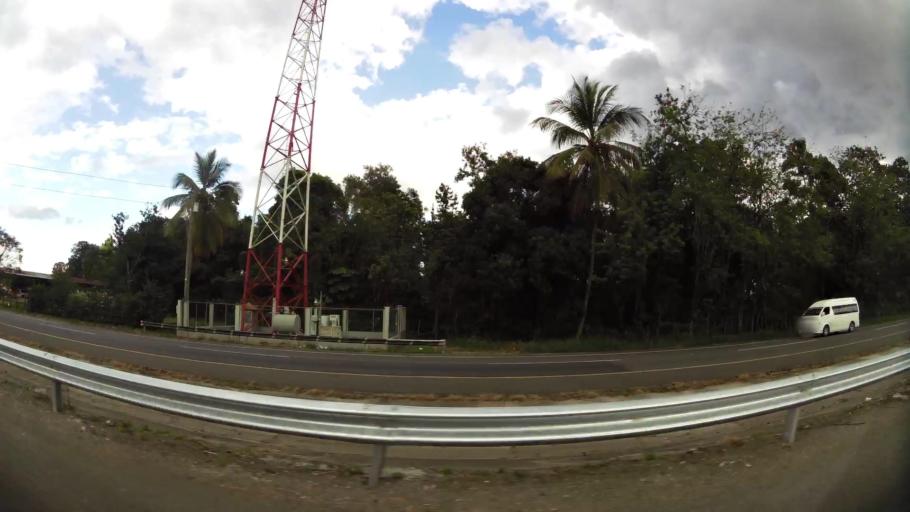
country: DO
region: Monsenor Nouel
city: Sabana del Puerto
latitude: 19.0720
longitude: -70.4458
